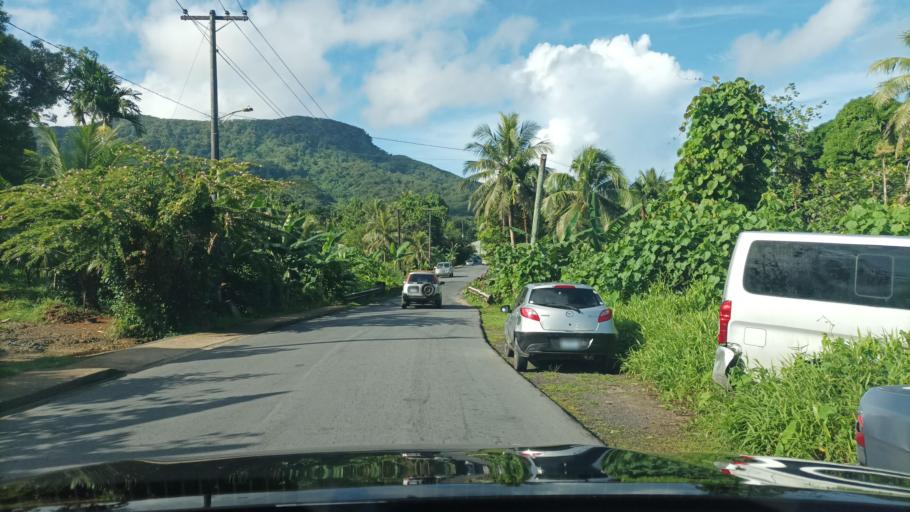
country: FM
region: Pohnpei
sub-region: Sokehs Municipality
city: Palikir - National Government Center
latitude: 6.9393
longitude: 158.1842
